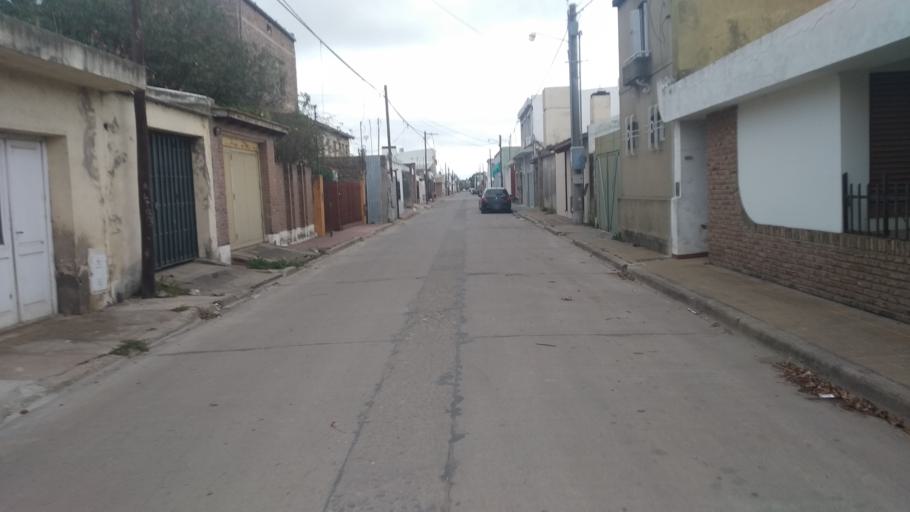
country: AR
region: Cordoba
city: Leones
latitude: -32.6615
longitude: -62.3000
